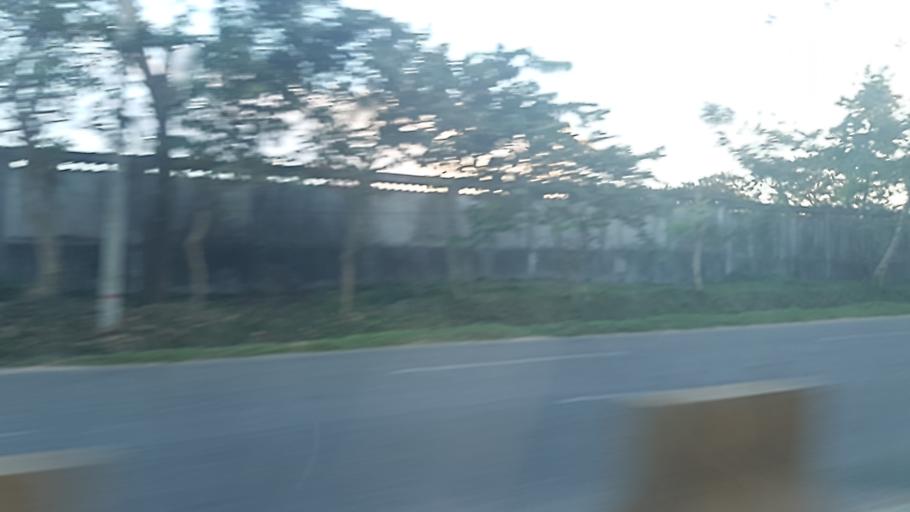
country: MM
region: Yangon
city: Yangon
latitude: 16.9100
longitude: 96.1311
